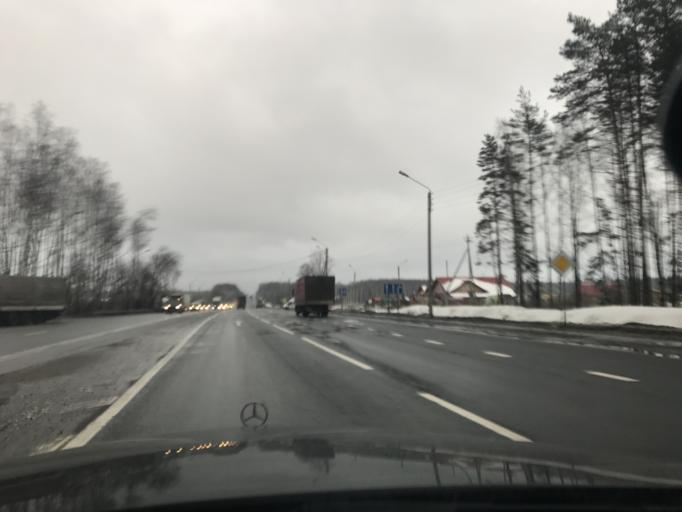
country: RU
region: Vladimir
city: Melekhovo
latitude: 56.2076
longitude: 41.2293
